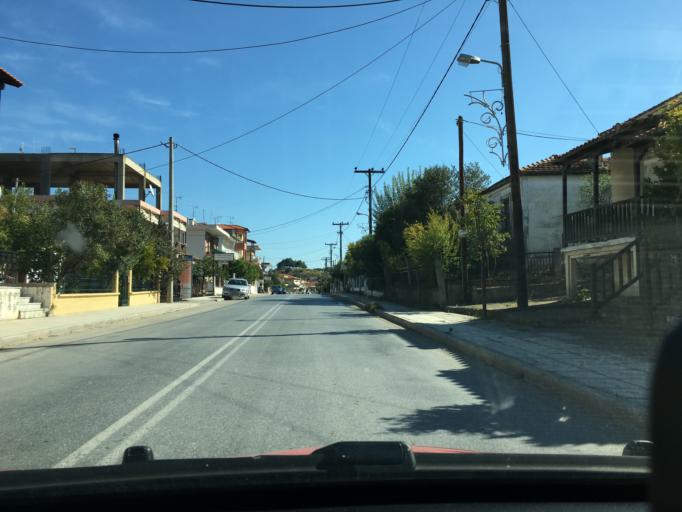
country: GR
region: Central Macedonia
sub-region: Nomos Chalkidikis
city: Ierissos
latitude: 40.3968
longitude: 23.8778
